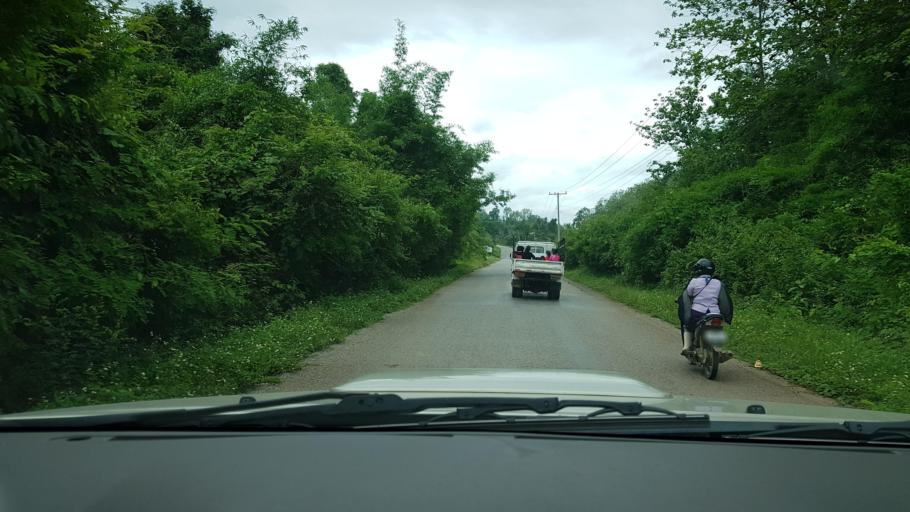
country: LA
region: Loungnamtha
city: Muang Nale
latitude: 20.3134
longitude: 101.6532
